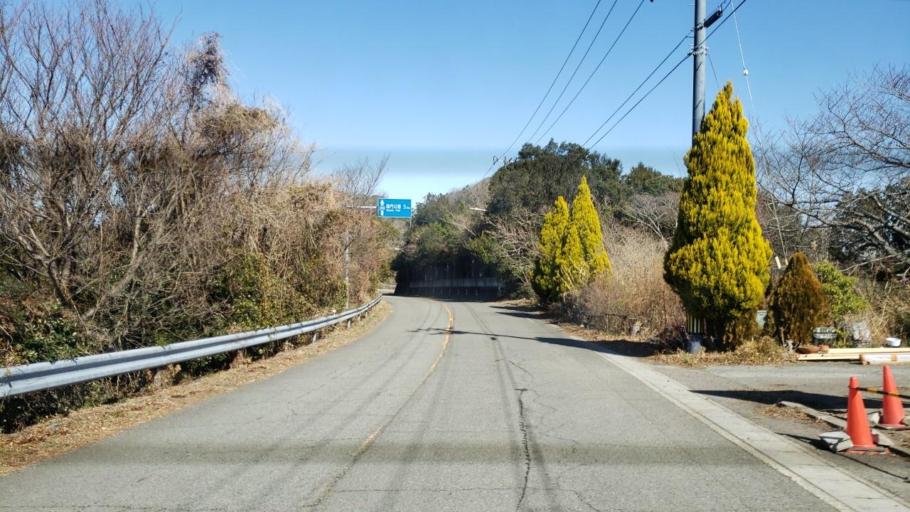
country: JP
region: Tokushima
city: Narutocho-mitsuishi
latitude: 34.2333
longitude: 134.6036
